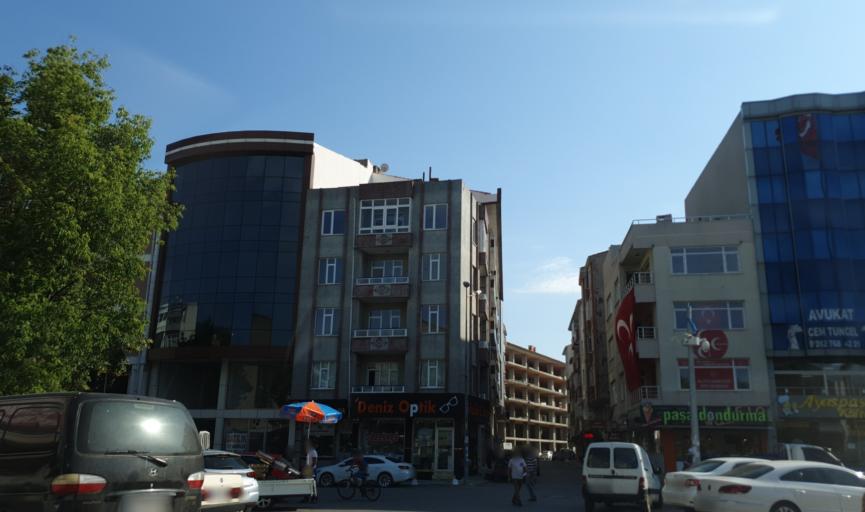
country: TR
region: Tekirdag
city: Saray
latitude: 41.4415
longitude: 27.9198
